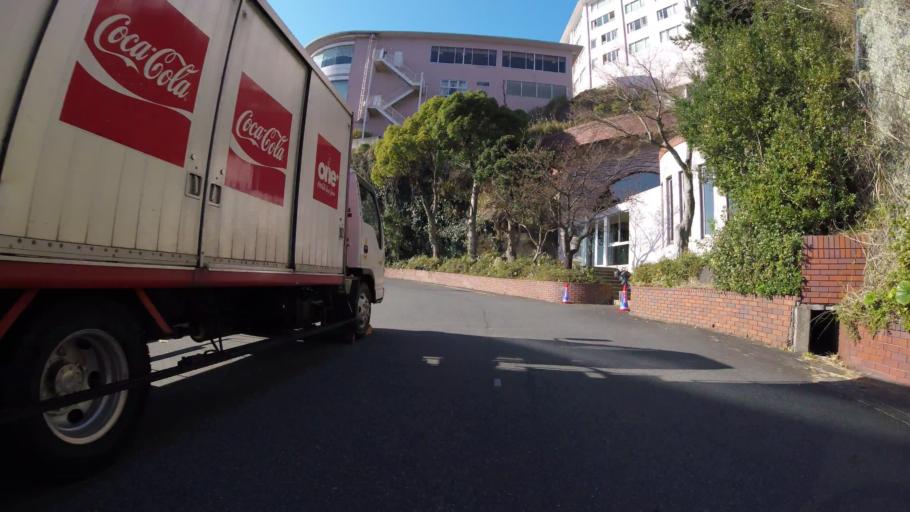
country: JP
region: Shizuoka
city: Atami
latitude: 35.0860
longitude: 139.0808
